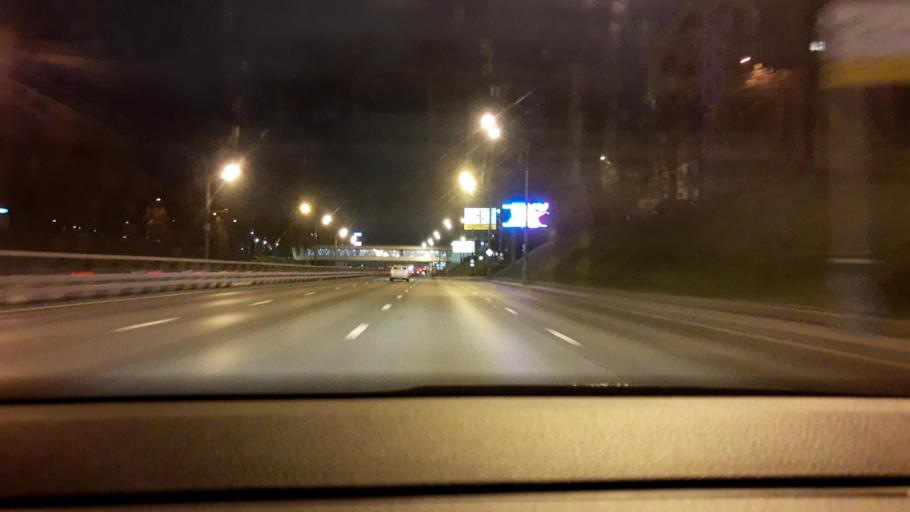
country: RU
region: Moscow
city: Rostokino
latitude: 55.8380
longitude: 37.6618
